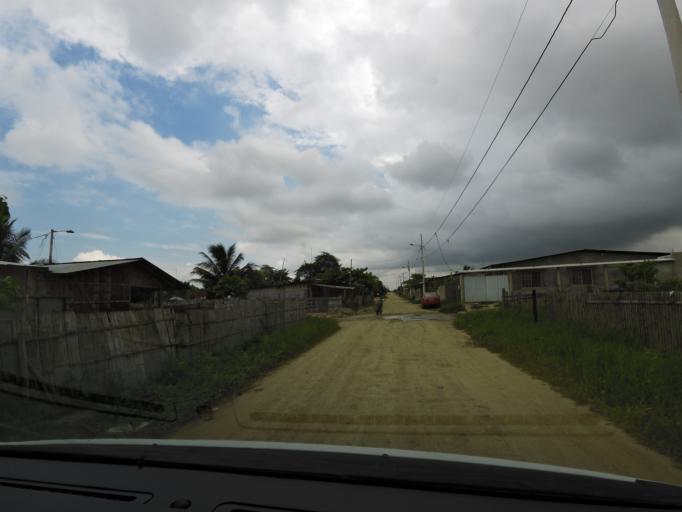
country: EC
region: El Oro
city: Huaquillas
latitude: -3.4855
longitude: -80.2057
